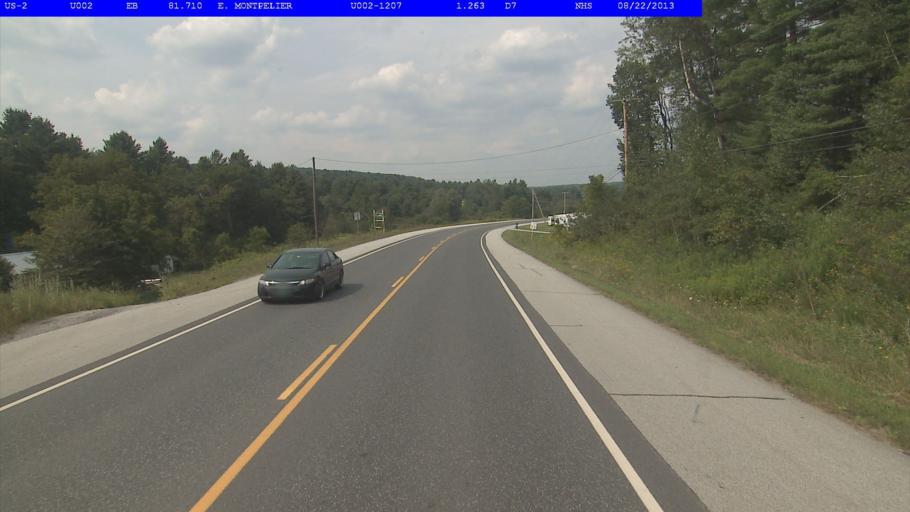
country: US
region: Vermont
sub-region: Washington County
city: Barre
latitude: 44.2513
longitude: -72.5016
